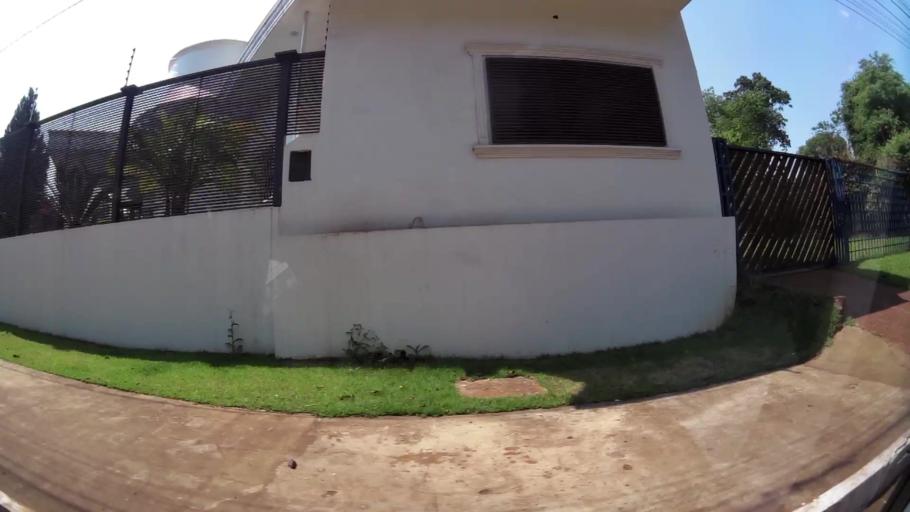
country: PY
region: Alto Parana
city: Presidente Franco
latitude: -25.5239
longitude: -54.6251
